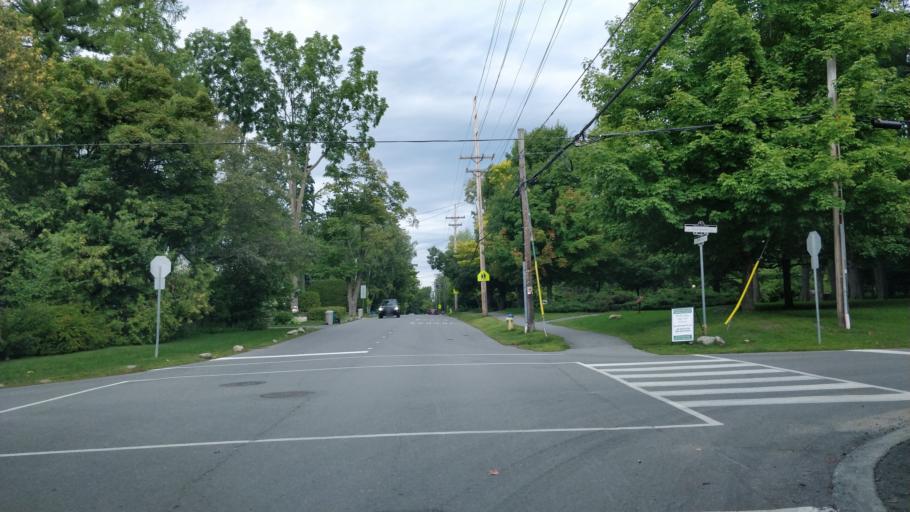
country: CA
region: Quebec
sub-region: Outaouais
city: Gatineau
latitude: 45.4481
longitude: -75.6784
